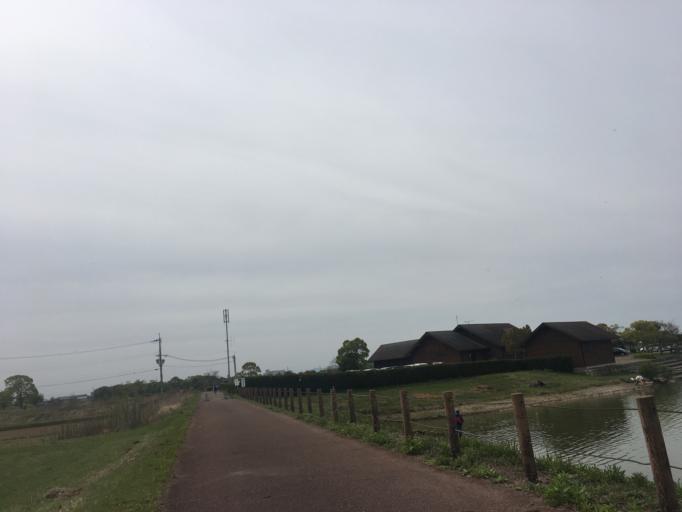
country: JP
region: Hyogo
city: Miki
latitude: 34.7678
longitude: 134.9251
